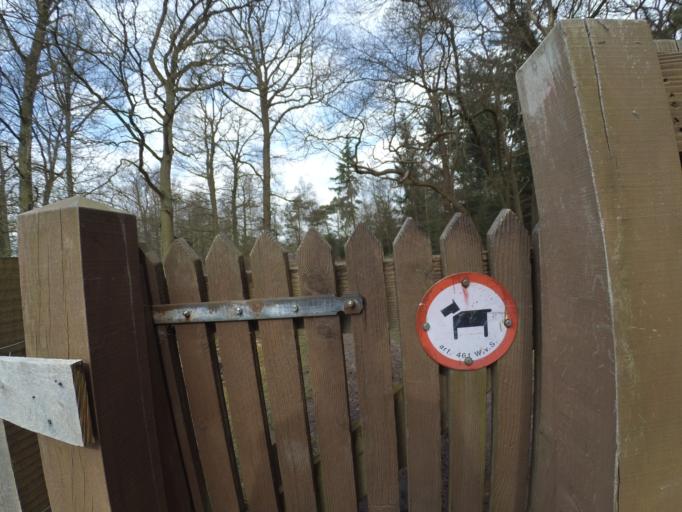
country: NL
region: Utrecht
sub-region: Gemeente Amersfoort
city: Randenbroek
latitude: 52.1120
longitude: 5.3776
